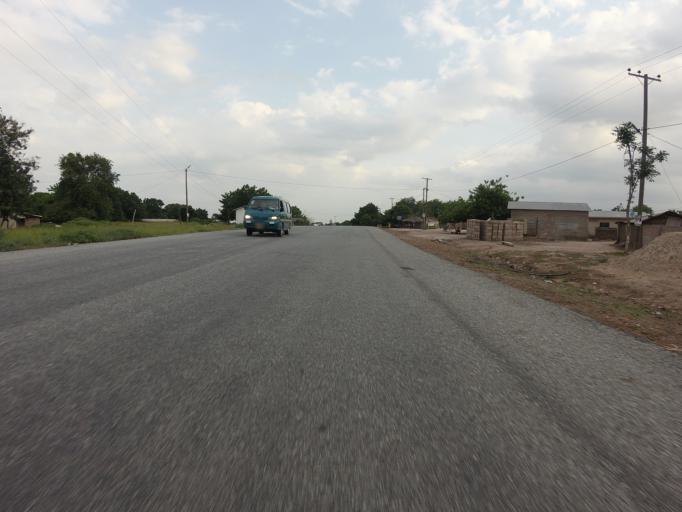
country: GH
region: Volta
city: Ho
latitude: 6.3941
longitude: 0.5259
